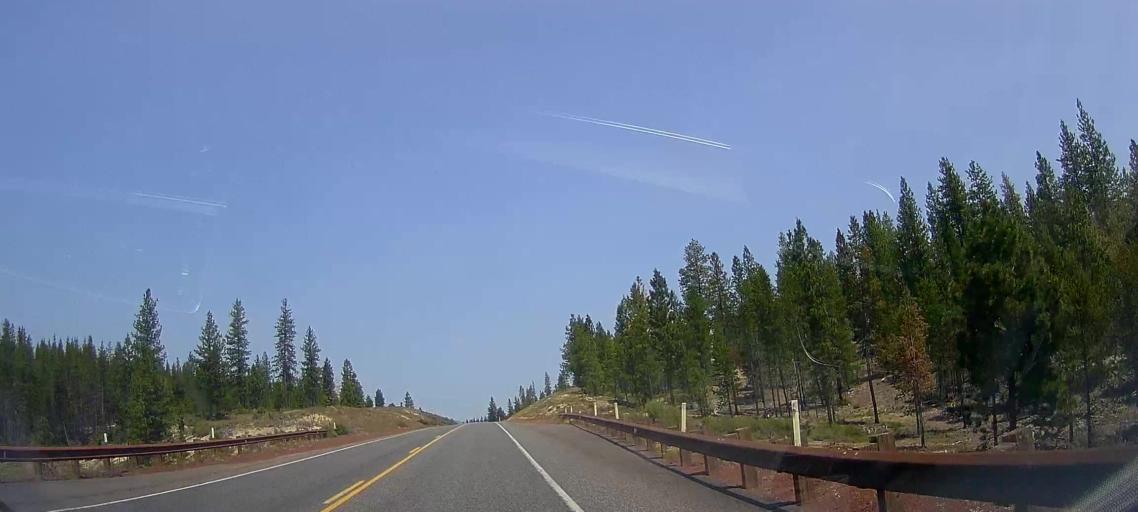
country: US
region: Oregon
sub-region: Deschutes County
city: La Pine
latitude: 43.4219
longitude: -121.7168
